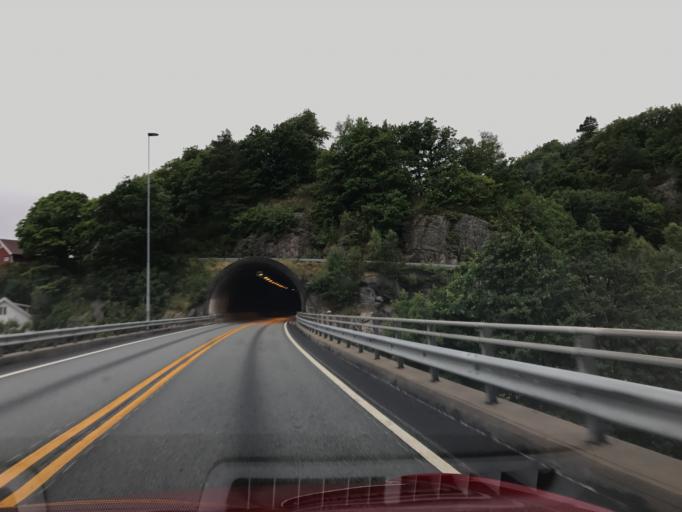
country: NO
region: Vest-Agder
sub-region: Mandal
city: Mandal
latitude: 58.0306
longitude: 7.4692
